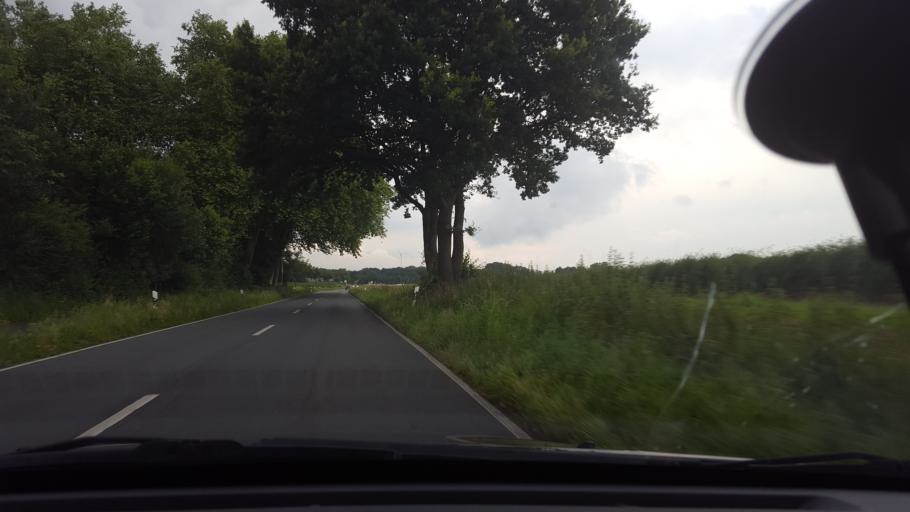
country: DE
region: North Rhine-Westphalia
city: Herten
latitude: 51.6327
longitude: 7.1569
